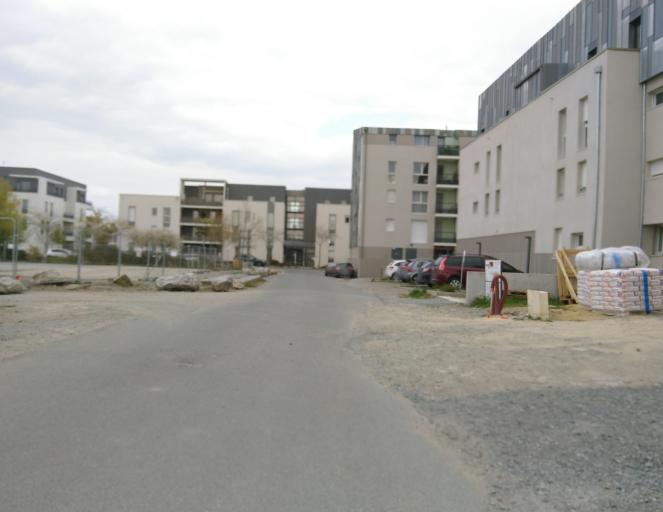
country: FR
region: Pays de la Loire
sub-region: Departement de Maine-et-Loire
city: Les Ponts-de-Ce
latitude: 47.4463
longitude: -0.5129
